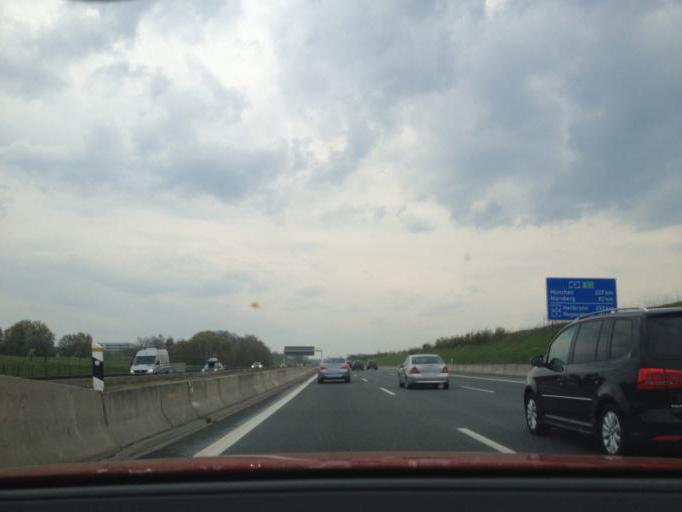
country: DE
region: Bavaria
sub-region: Upper Franconia
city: Bayreuth
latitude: 49.9260
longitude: 11.6025
